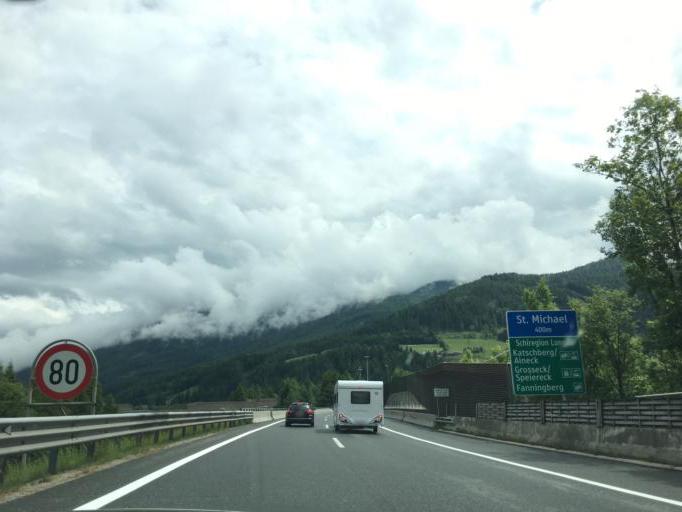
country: AT
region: Salzburg
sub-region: Politischer Bezirk Tamsweg
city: Sankt Michael im Lungau
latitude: 47.0974
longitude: 13.6063
